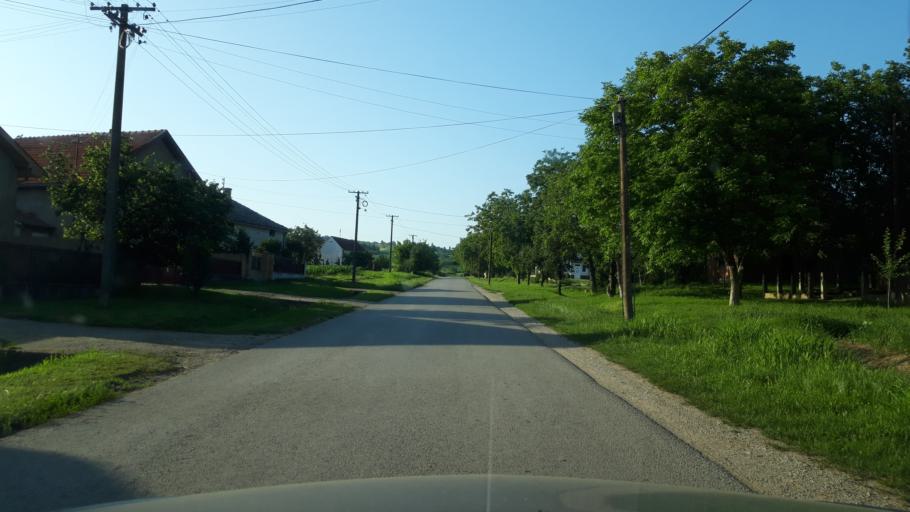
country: RS
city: Celarevo
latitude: 45.1166
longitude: 19.5093
